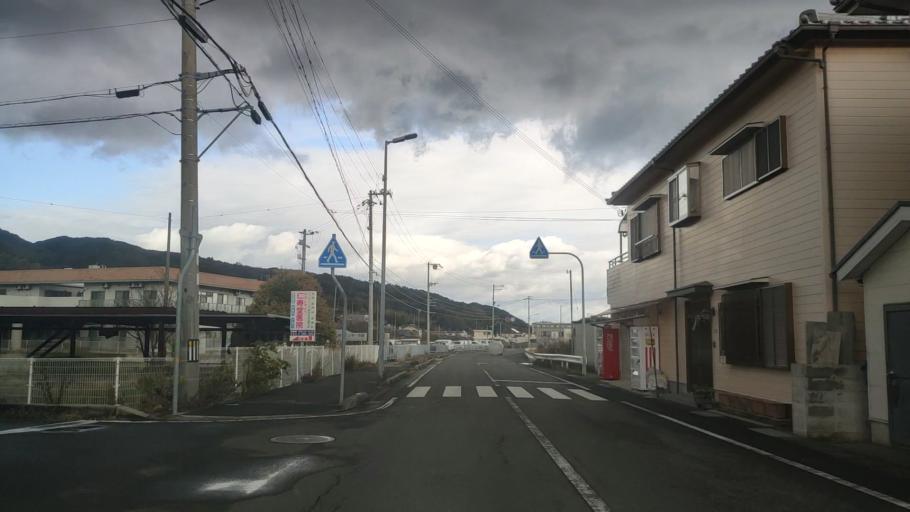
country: JP
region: Hyogo
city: Sumoto
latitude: 34.3311
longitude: 134.8650
